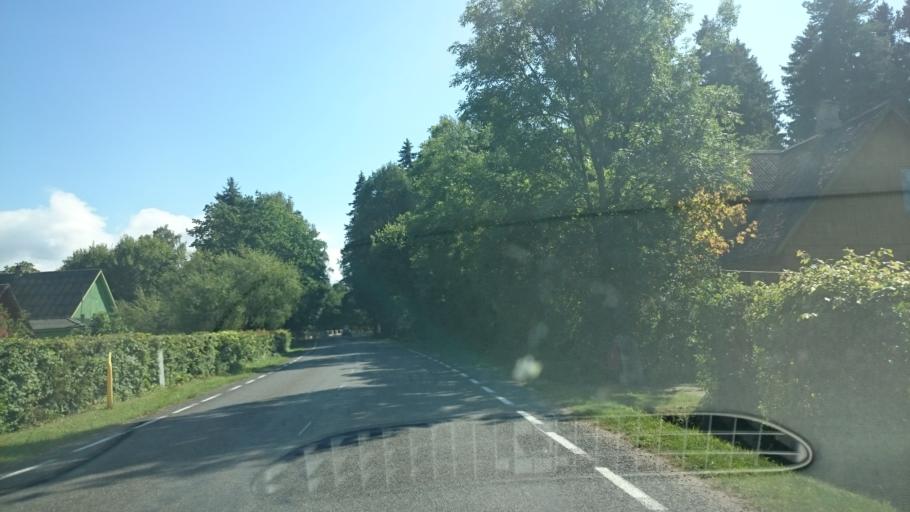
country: EE
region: Saare
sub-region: Kuressaare linn
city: Kuressaare
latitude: 58.5751
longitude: 22.6861
